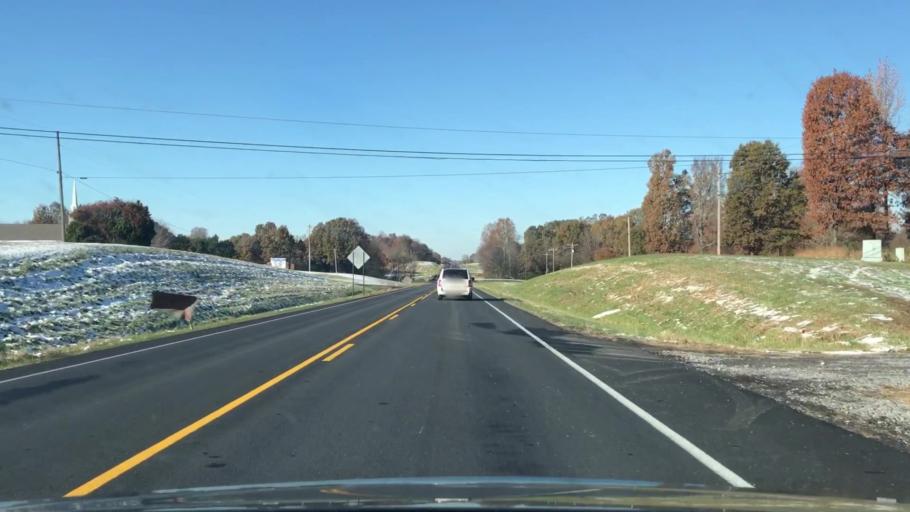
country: US
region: Kentucky
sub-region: Livingston County
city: Ledbetter
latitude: 37.0066
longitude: -88.4495
